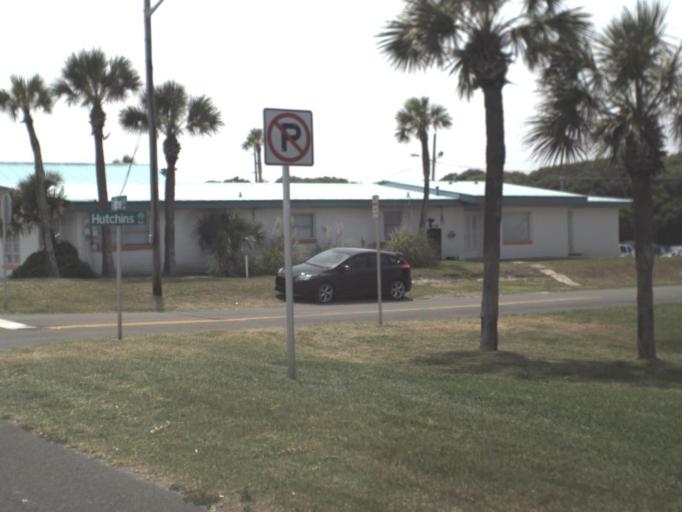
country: US
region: Florida
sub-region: Nassau County
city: Fernandina Beach
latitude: 30.6224
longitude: -81.4406
